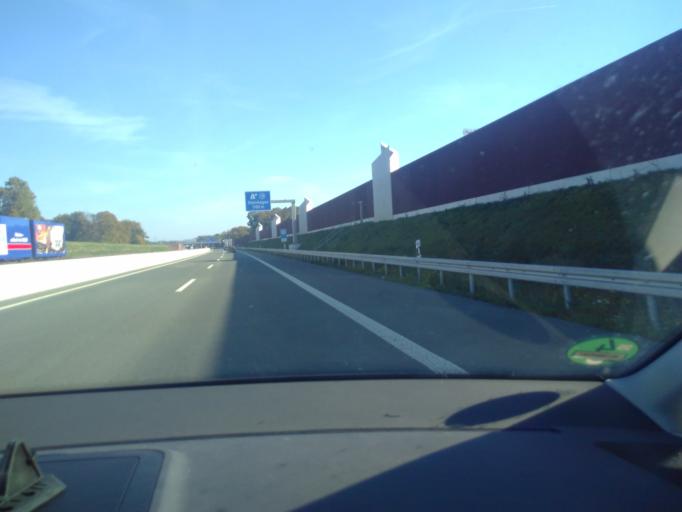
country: DE
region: North Rhine-Westphalia
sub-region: Regierungsbezirk Detmold
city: Steinhagen
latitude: 52.0137
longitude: 8.4068
